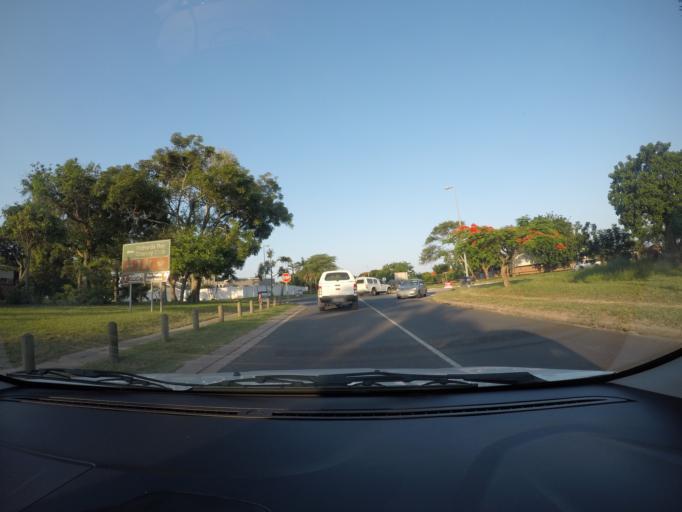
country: ZA
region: KwaZulu-Natal
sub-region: uThungulu District Municipality
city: Richards Bay
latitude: -28.7781
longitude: 32.1007
